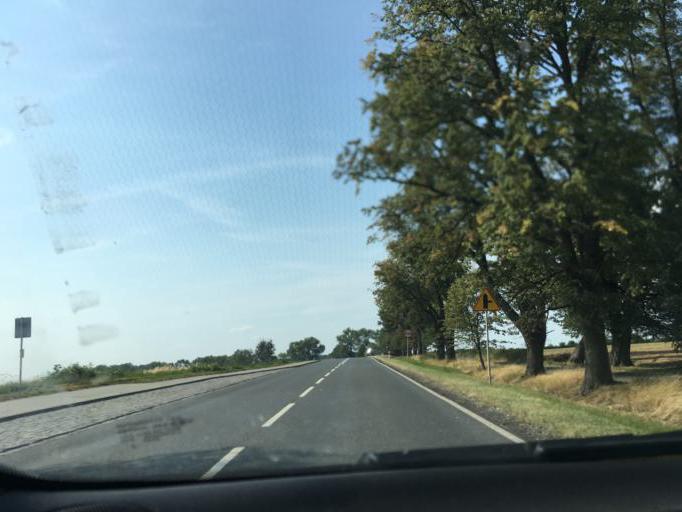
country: PL
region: Opole Voivodeship
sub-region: Powiat prudnicki
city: Laka Prudnicka
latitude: 50.4174
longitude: 17.4848
